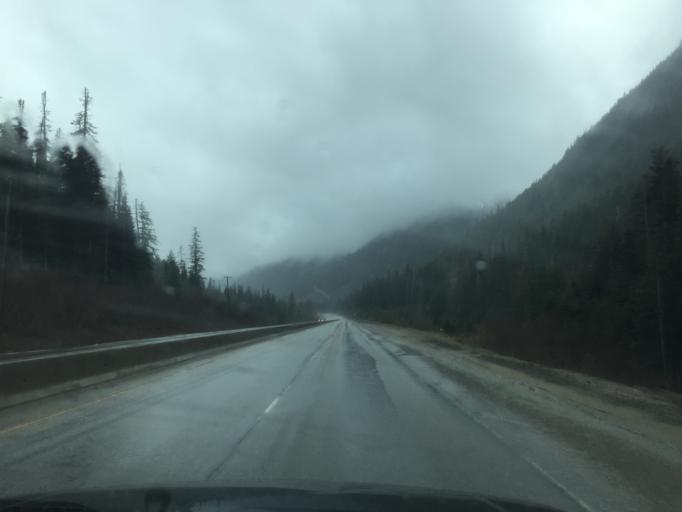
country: CA
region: British Columbia
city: Hope
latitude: 49.5857
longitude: -121.1675
